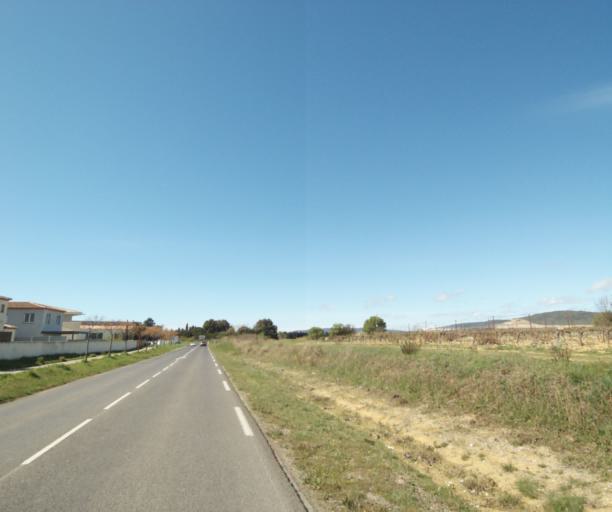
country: FR
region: Languedoc-Roussillon
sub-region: Departement de l'Herault
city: Villeneuve-les-Maguelone
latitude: 43.5356
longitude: 3.8536
